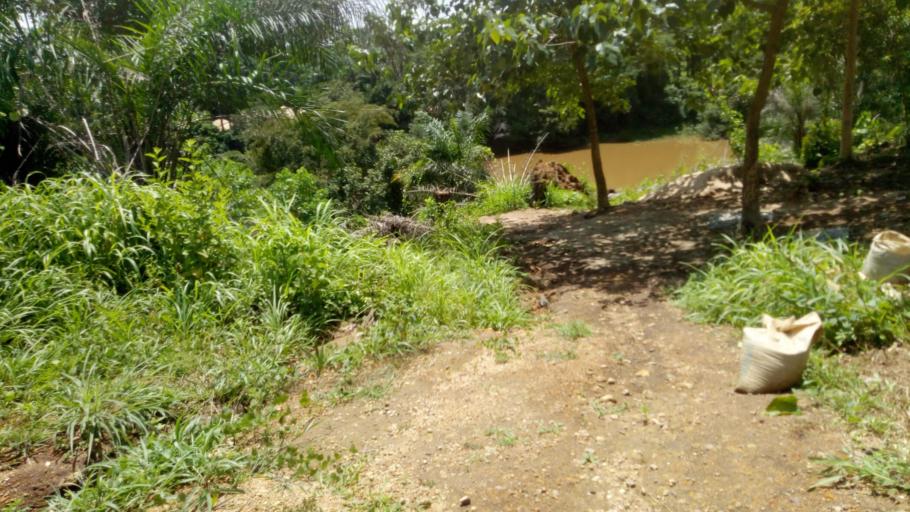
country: SL
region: Northern Province
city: Magburaka
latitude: 8.7231
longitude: -11.9579
